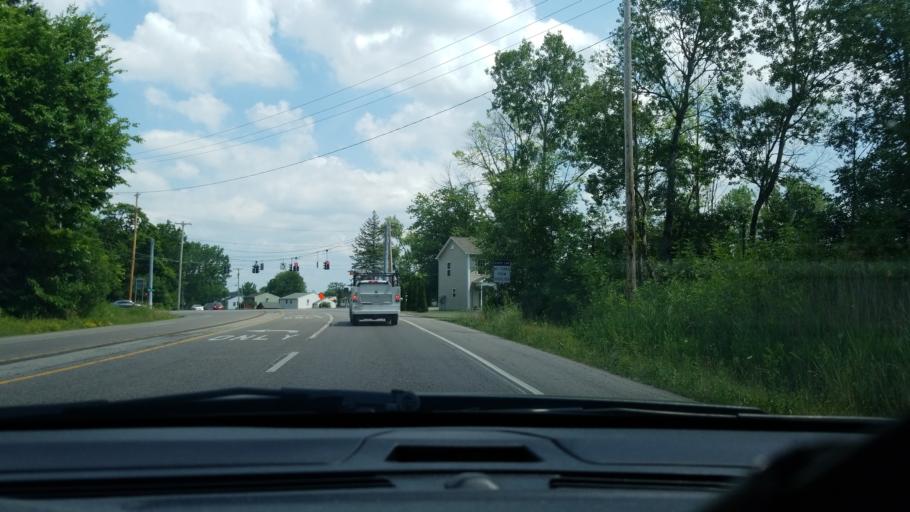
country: US
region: New York
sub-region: Onondaga County
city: Liverpool
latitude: 43.1495
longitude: -76.1894
